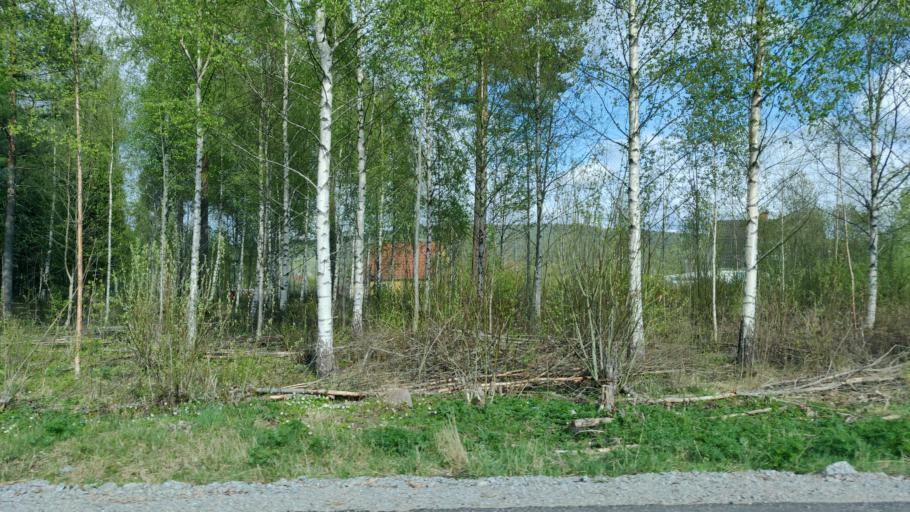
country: SE
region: Vaermland
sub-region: Hagfors Kommun
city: Hagfors
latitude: 60.0195
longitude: 13.6768
